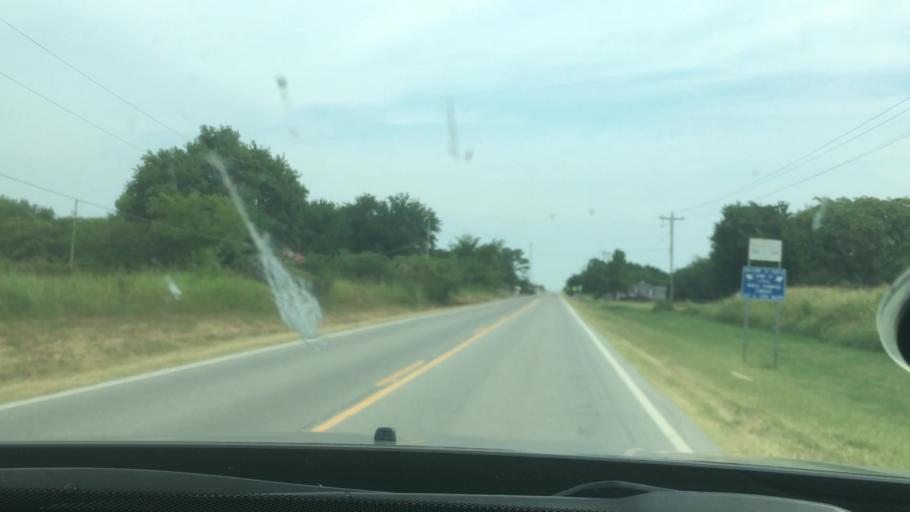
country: US
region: Oklahoma
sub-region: Coal County
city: Coalgate
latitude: 34.5987
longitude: -96.4244
